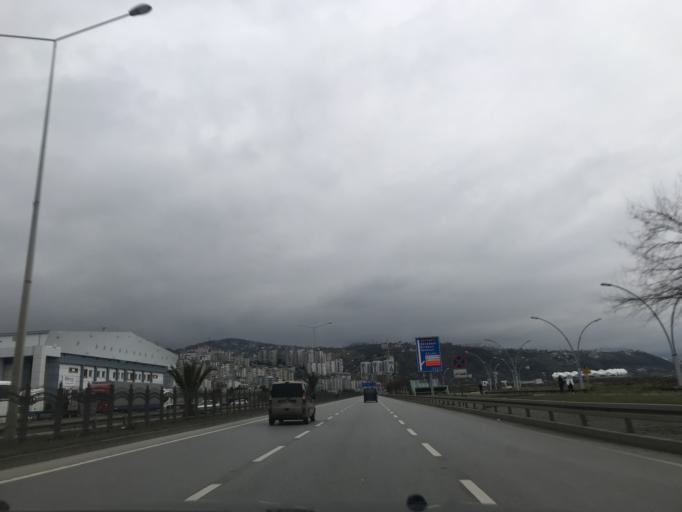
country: TR
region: Trabzon
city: Trabzon
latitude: 40.9980
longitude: 39.6739
